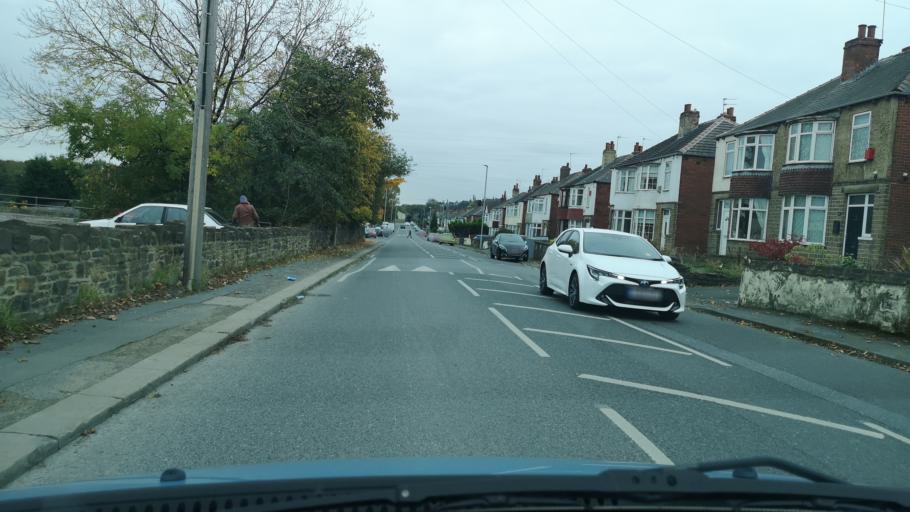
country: GB
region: England
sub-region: Kirklees
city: Dewsbury
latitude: 53.6743
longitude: -1.6532
